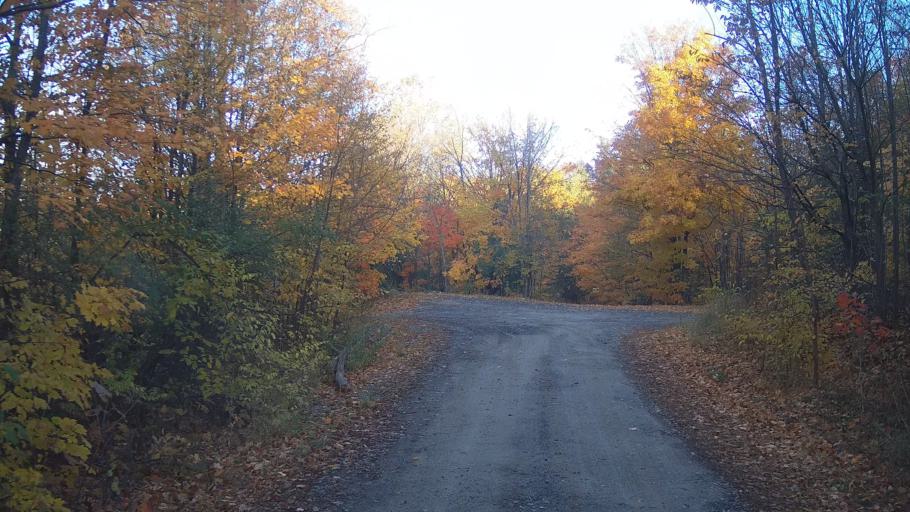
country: CA
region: Ontario
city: Arnprior
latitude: 45.3325
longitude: -76.3698
